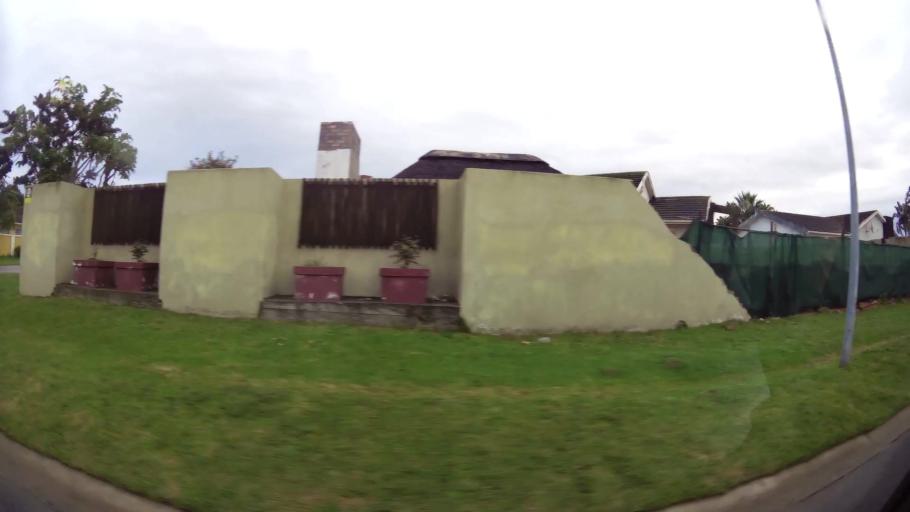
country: ZA
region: Eastern Cape
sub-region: Nelson Mandela Bay Metropolitan Municipality
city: Port Elizabeth
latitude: -33.9934
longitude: 25.5516
